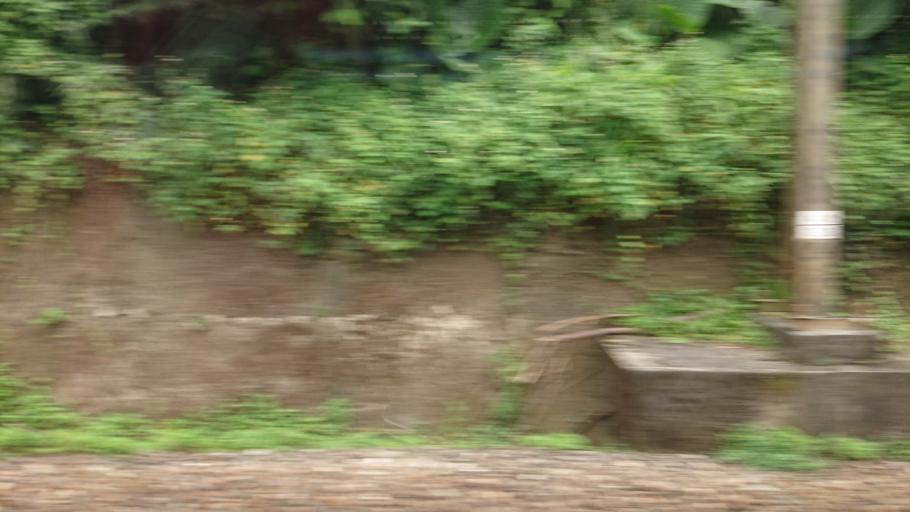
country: TW
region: Taiwan
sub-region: Keelung
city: Keelung
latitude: 24.9526
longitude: 121.9129
